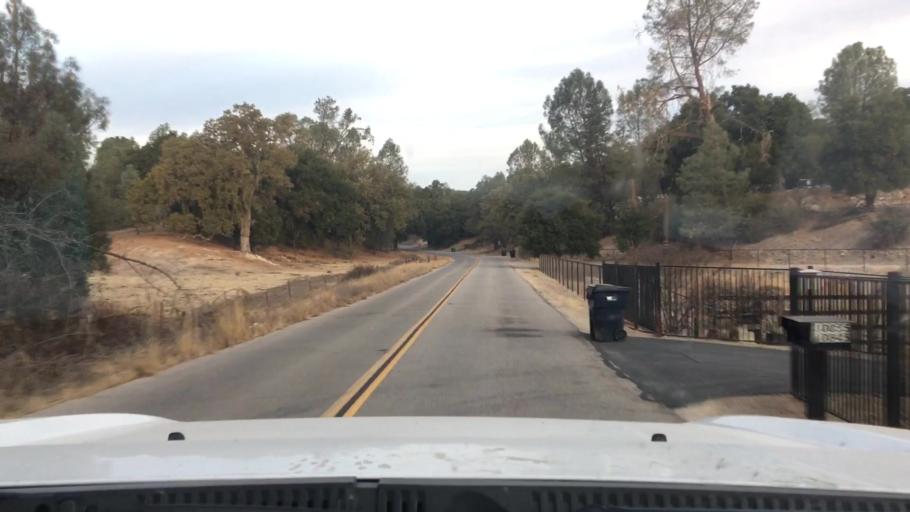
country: US
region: California
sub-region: San Luis Obispo County
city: Atascadero
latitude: 35.4498
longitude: -120.6515
